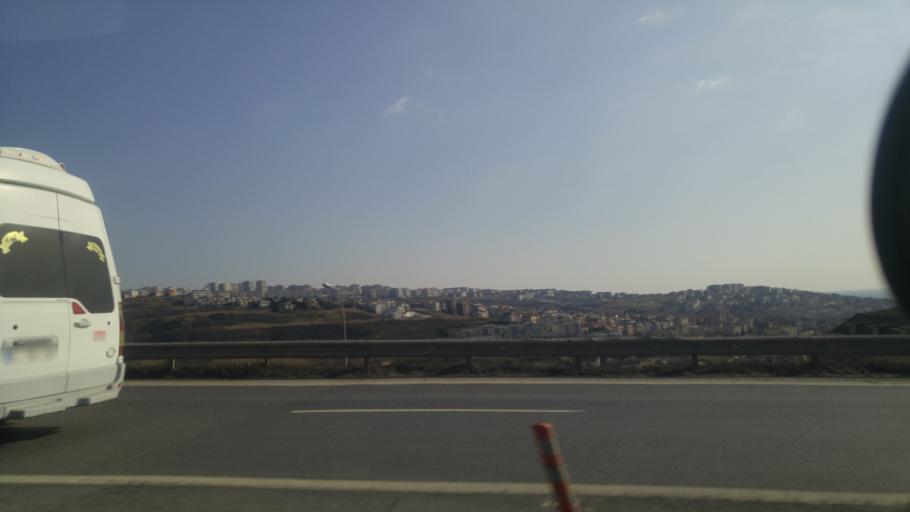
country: TR
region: Istanbul
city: Bueyuekcekmece
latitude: 41.0252
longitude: 28.6073
